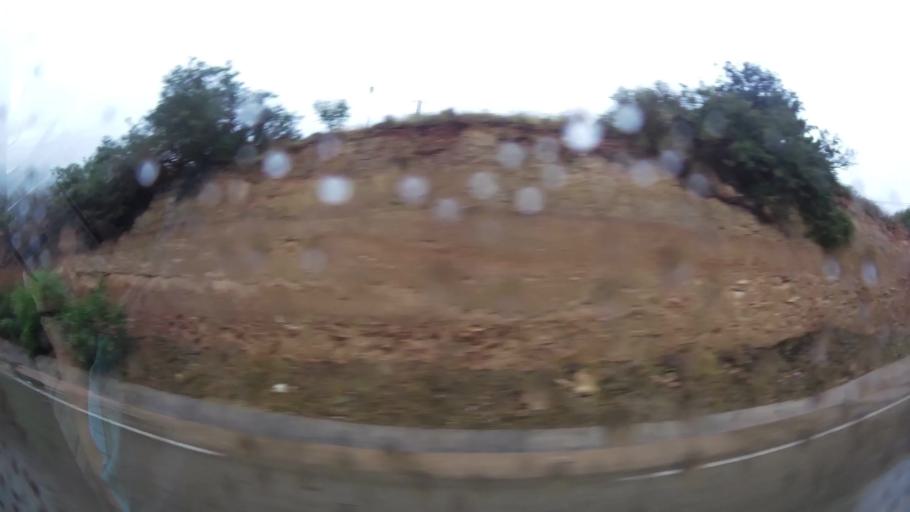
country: MA
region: Taza-Al Hoceima-Taounate
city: Tirhanimine
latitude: 35.2231
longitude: -3.9283
